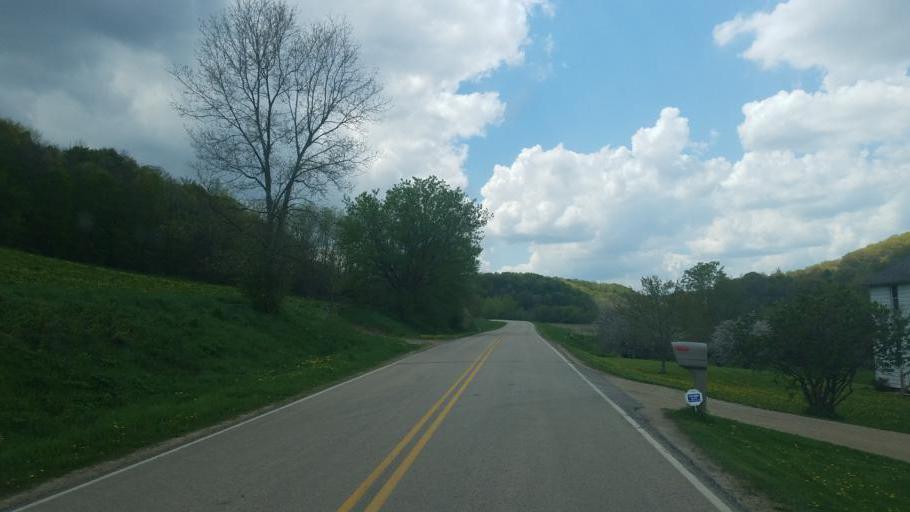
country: US
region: Wisconsin
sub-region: Vernon County
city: Hillsboro
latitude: 43.6098
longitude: -90.2843
